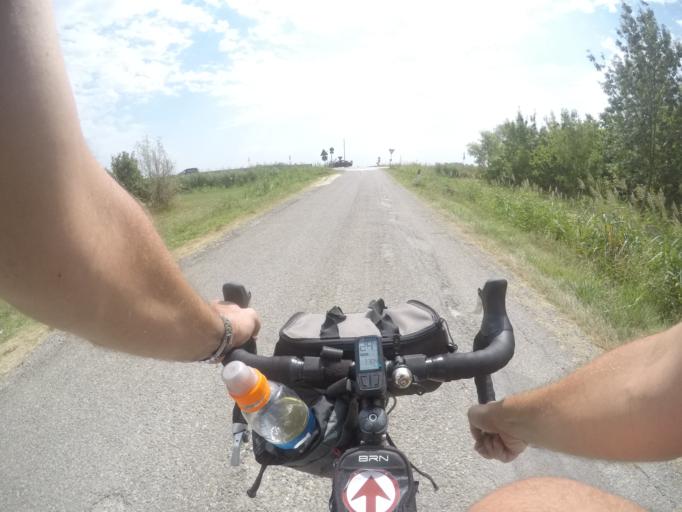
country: IT
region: Emilia-Romagna
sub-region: Provincia di Ravenna
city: Marina Romea
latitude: 44.5765
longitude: 12.2540
